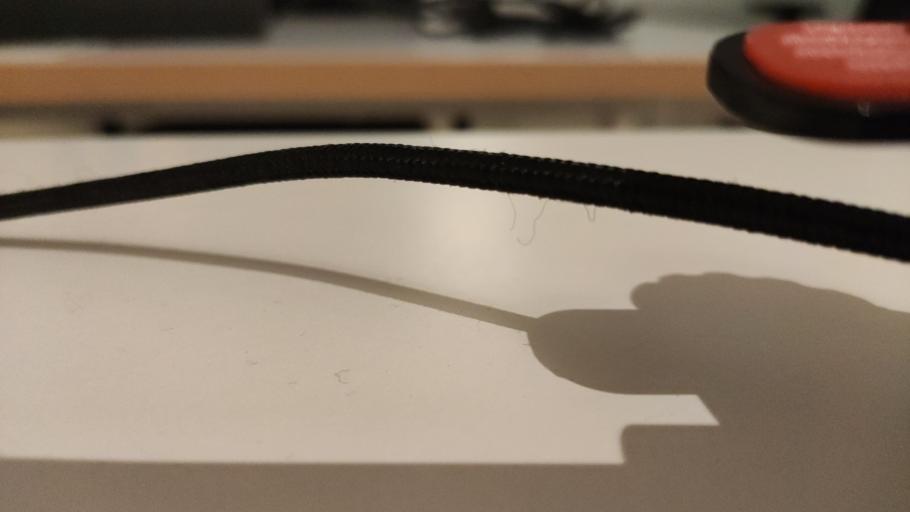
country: RU
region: Moskovskaya
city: Malaya Dubna
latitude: 55.8535
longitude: 38.9629
